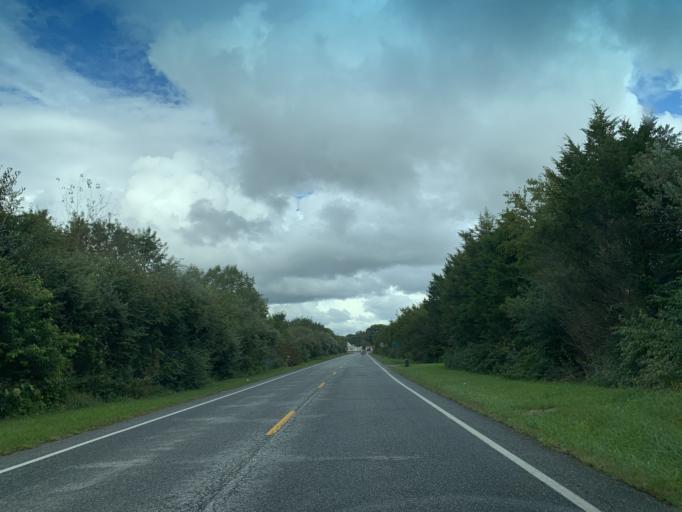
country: US
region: Maryland
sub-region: Caroline County
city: Greensboro
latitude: 39.0568
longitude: -75.8482
